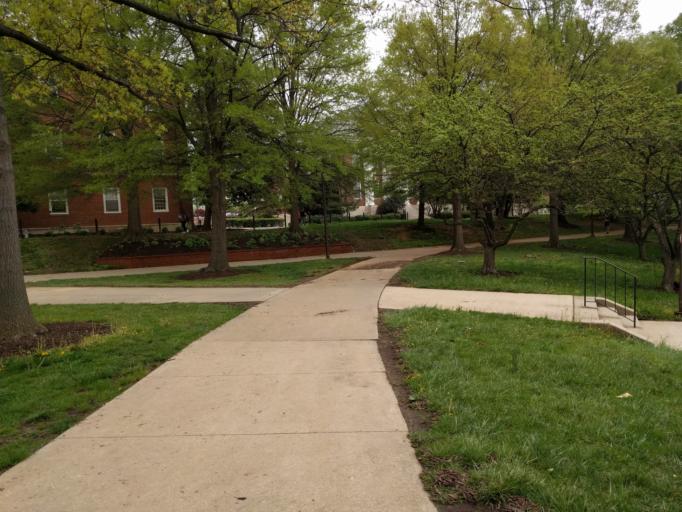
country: US
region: Maryland
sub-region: Prince George's County
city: College Park
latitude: 38.9863
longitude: -76.9446
